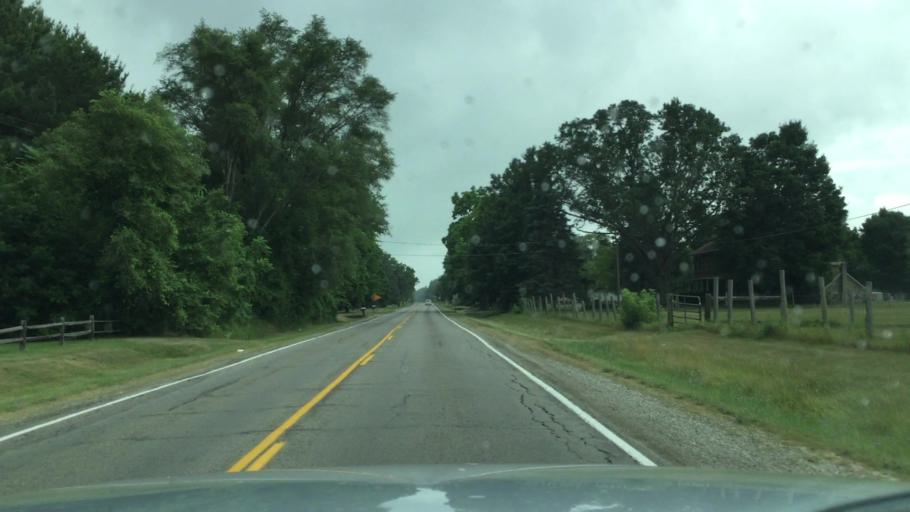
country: US
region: Michigan
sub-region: Genesee County
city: Clio
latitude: 43.1477
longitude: -83.7740
